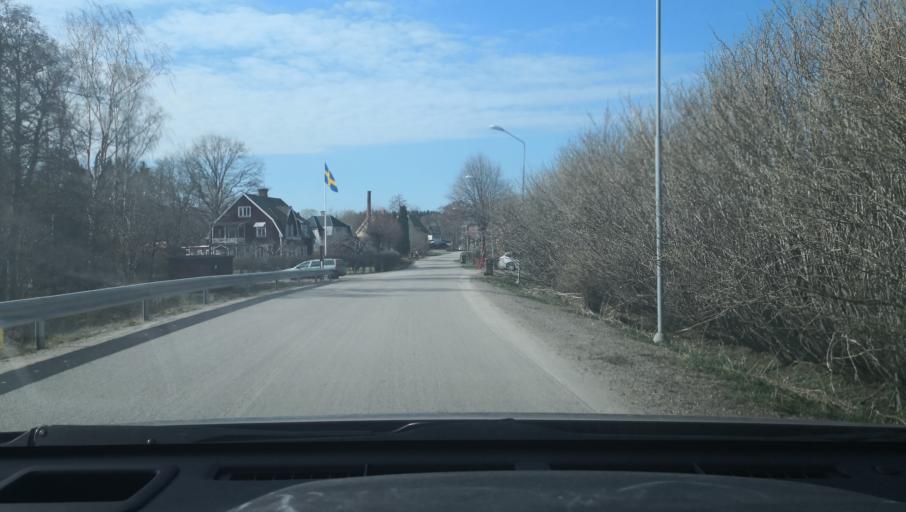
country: SE
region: Uppsala
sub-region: Heby Kommun
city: Morgongava
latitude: 59.8400
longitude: 16.9180
